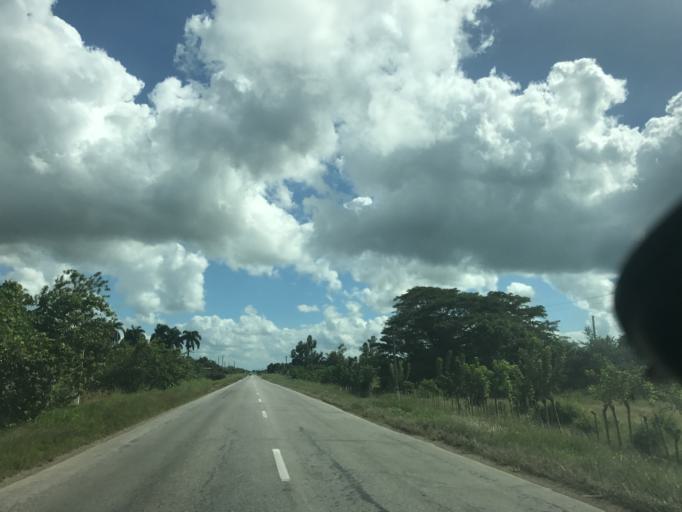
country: CU
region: Camaguey
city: Florida
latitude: 21.4812
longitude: -78.1803
